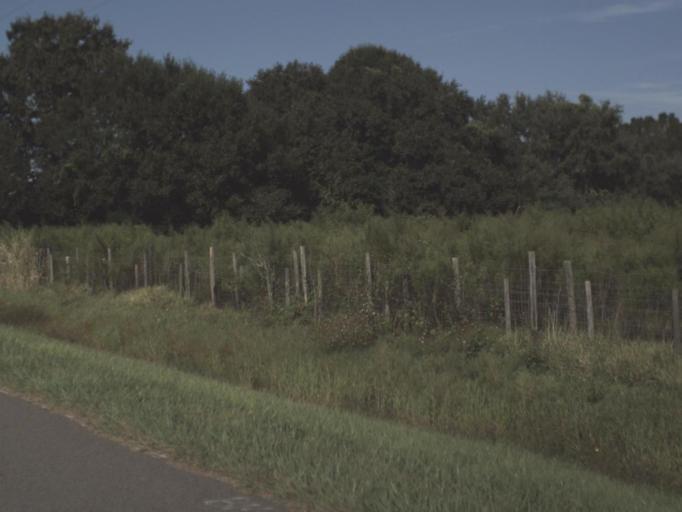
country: US
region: Florida
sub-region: Hardee County
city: Wauchula
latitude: 27.5515
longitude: -81.7065
